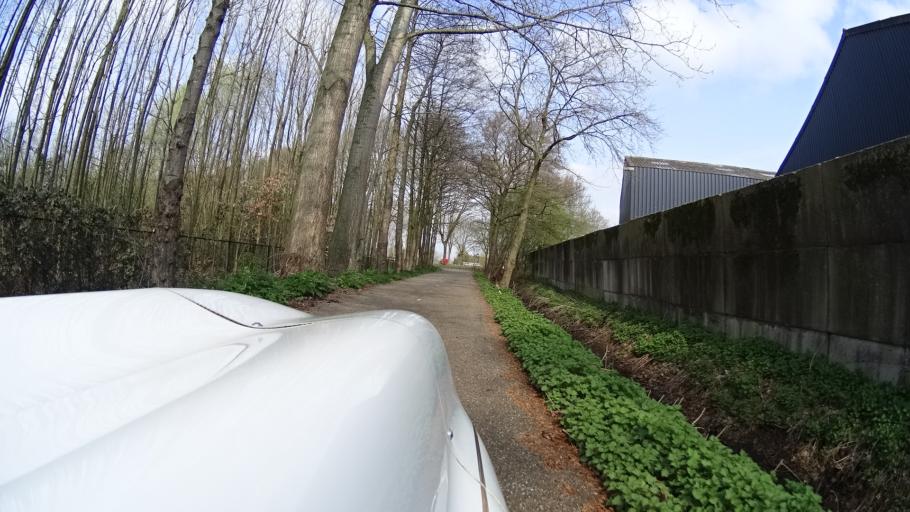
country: NL
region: North Brabant
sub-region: Gemeente Nuenen, Gerwen en Nederwetten
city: Nuenen
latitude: 51.5124
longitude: 5.5806
